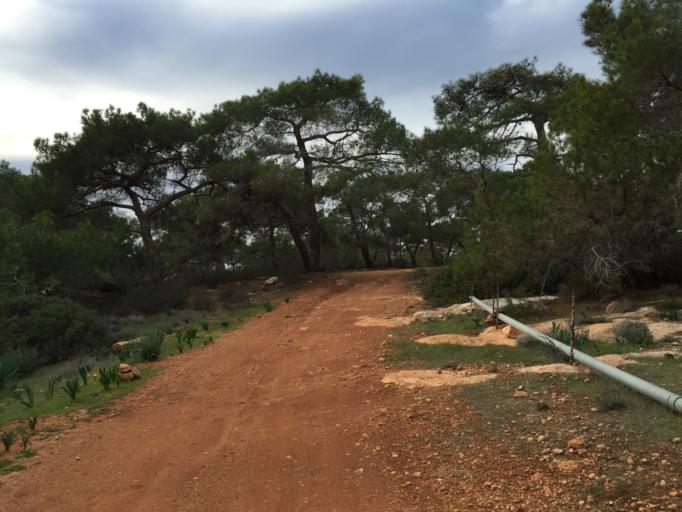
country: CY
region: Pafos
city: Pegeia
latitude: 34.8903
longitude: 32.3753
